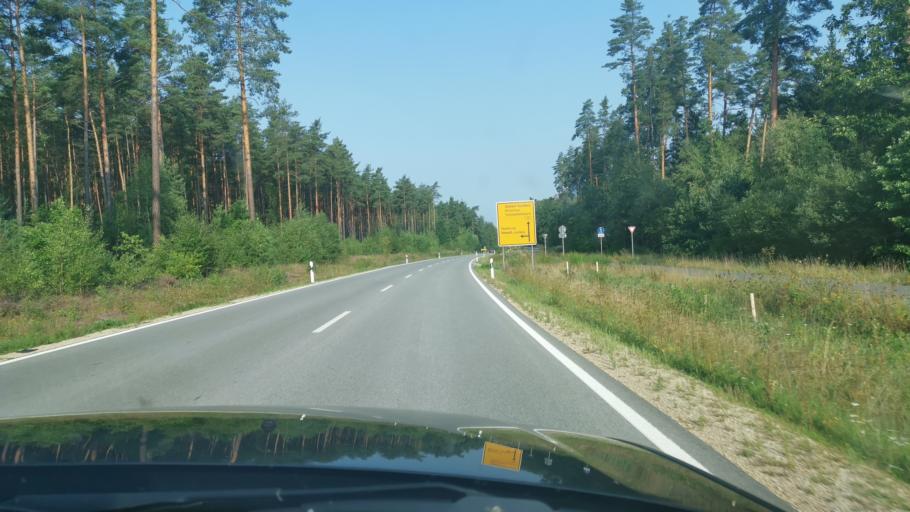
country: DE
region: Bavaria
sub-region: Upper Palatinate
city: Schnaittenbach
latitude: 49.5409
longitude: 12.0667
